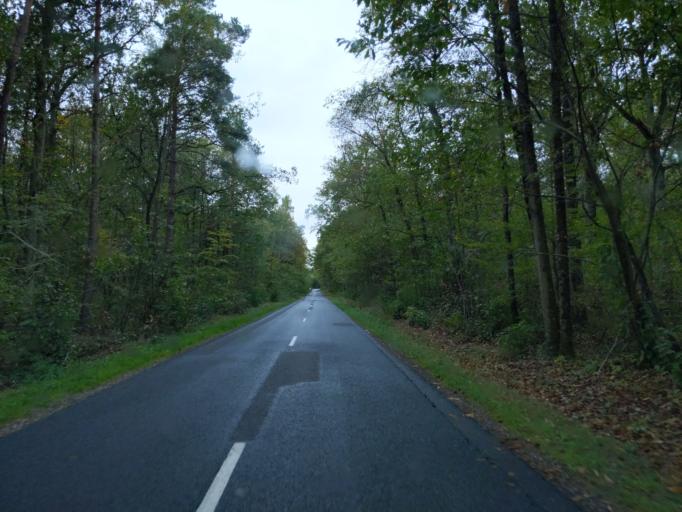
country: FR
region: Ile-de-France
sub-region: Departement des Yvelines
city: Saint-Arnoult-en-Yvelines
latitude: 48.5932
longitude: 1.9358
